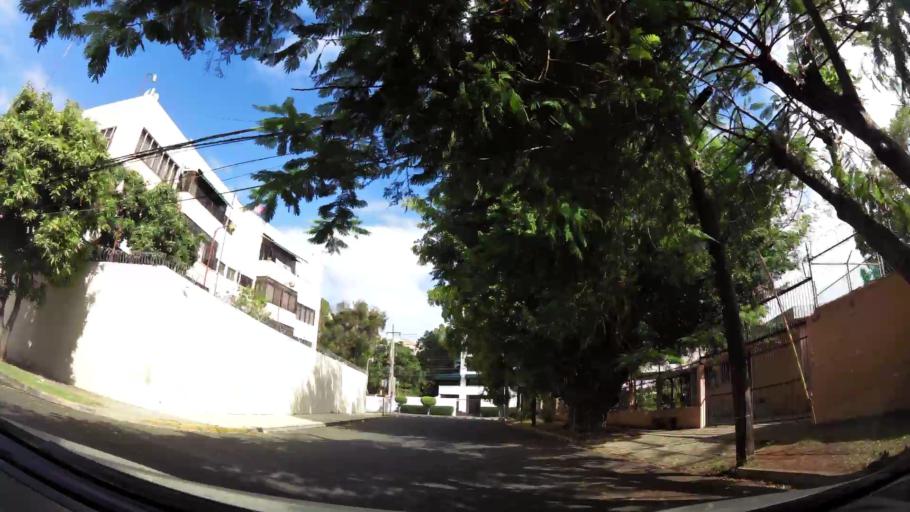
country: DO
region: Nacional
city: La Julia
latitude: 18.4631
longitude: -69.9260
